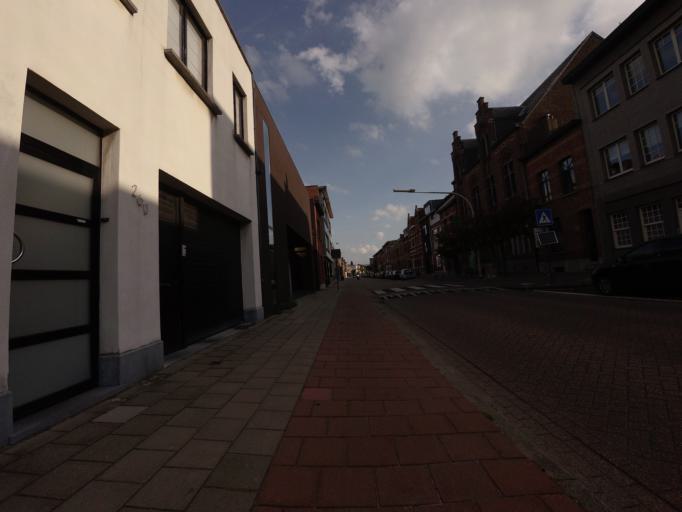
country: BE
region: Flanders
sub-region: Provincie Antwerpen
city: Antwerpen
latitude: 51.1782
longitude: 4.3924
